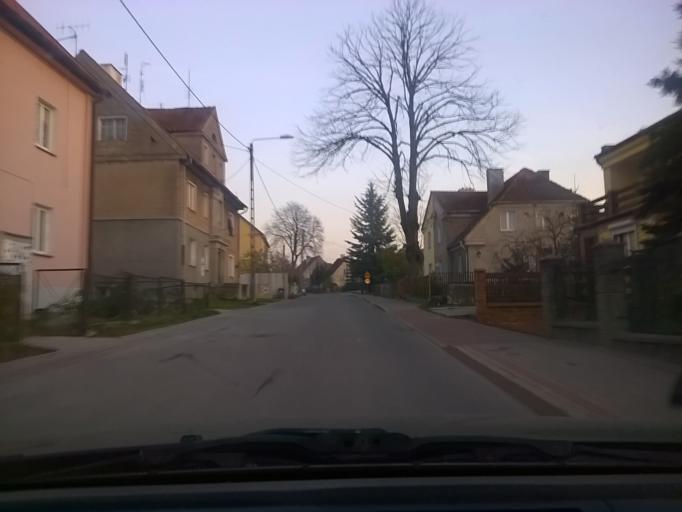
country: PL
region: Warmian-Masurian Voivodeship
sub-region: Powiat ketrzynski
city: Ketrzyn
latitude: 54.0803
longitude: 21.3587
